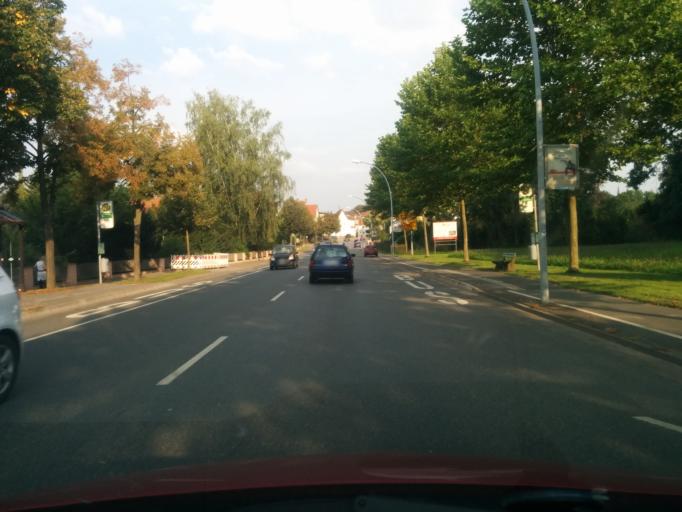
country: DE
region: Lower Saxony
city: Duderstadt
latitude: 51.5160
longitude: 10.2467
